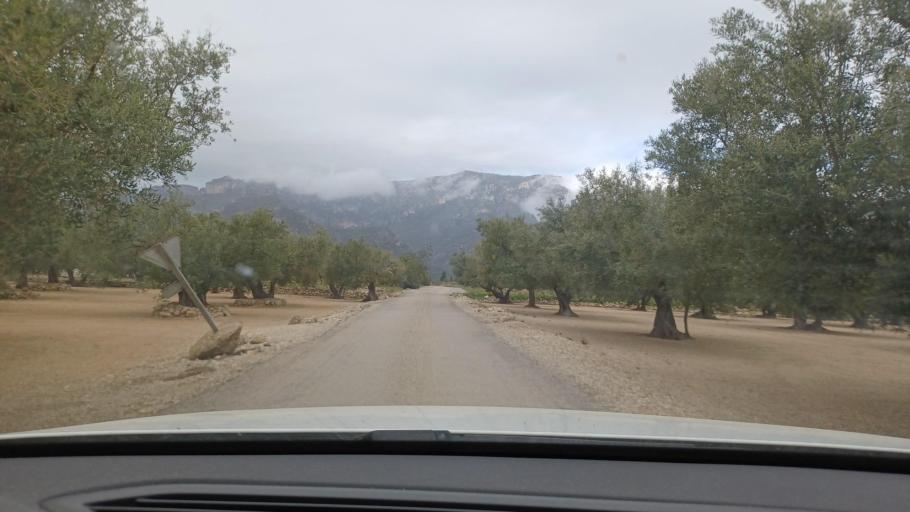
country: ES
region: Catalonia
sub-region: Provincia de Tarragona
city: Mas de Barberans
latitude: 40.7976
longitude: 0.4255
